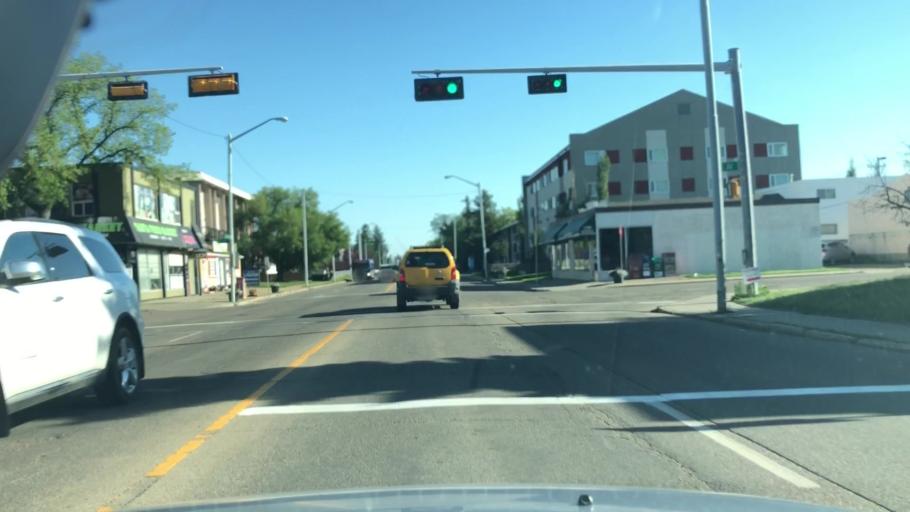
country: CA
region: Alberta
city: Edmonton
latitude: 53.5655
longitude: -113.5360
